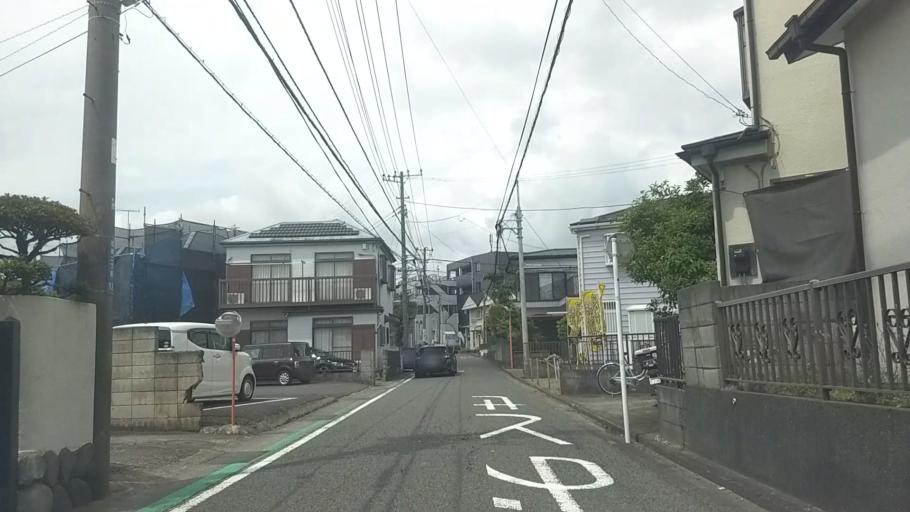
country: JP
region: Kanagawa
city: Fujisawa
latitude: 35.3456
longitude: 139.4556
